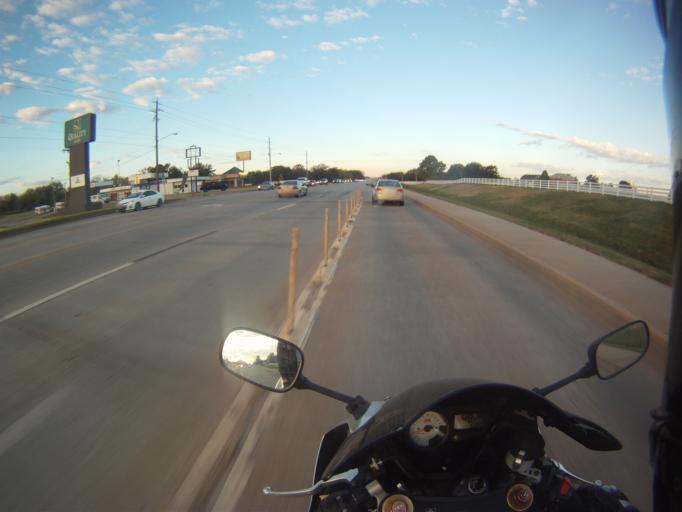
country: US
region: Oklahoma
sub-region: Payne County
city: Stillwater
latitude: 36.1159
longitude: -97.0905
